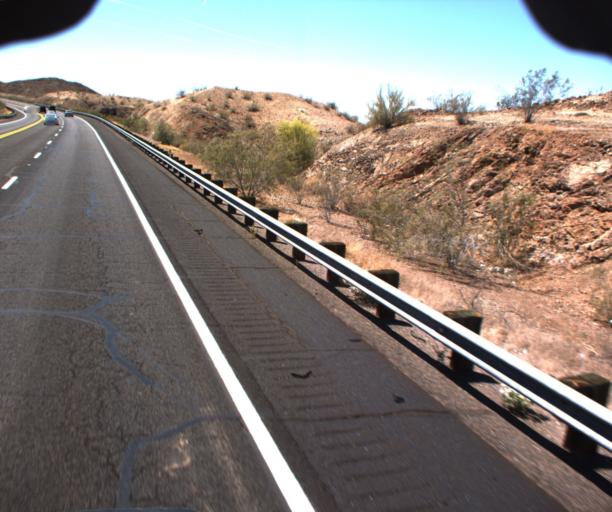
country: US
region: Arizona
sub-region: La Paz County
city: Cienega Springs
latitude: 34.2115
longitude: -114.2019
